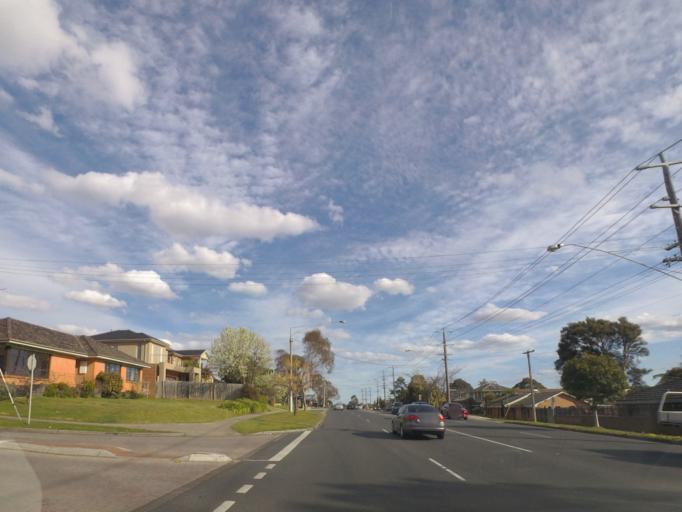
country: AU
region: Victoria
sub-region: Manningham
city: Doncaster East
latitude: -37.7928
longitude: 145.1428
